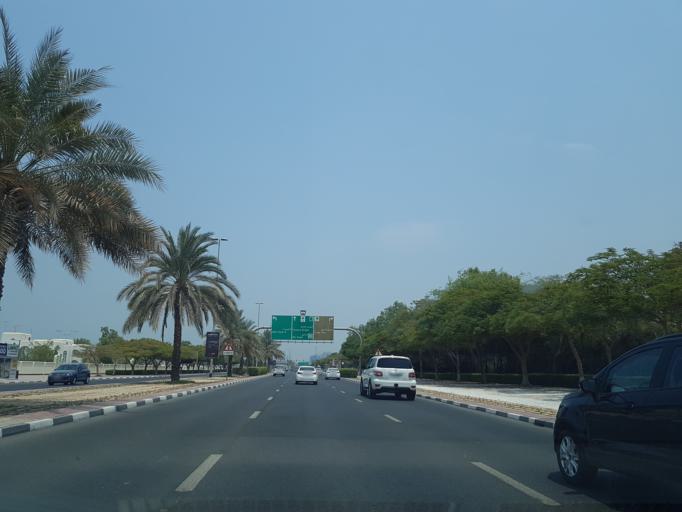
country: AE
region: Ash Shariqah
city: Sharjah
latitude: 25.2381
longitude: 55.3245
